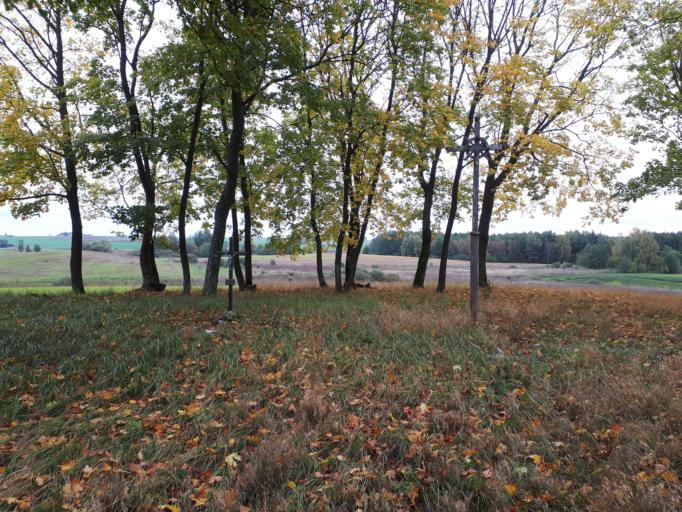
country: LT
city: Kalvarija
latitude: 54.4192
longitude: 23.3819
